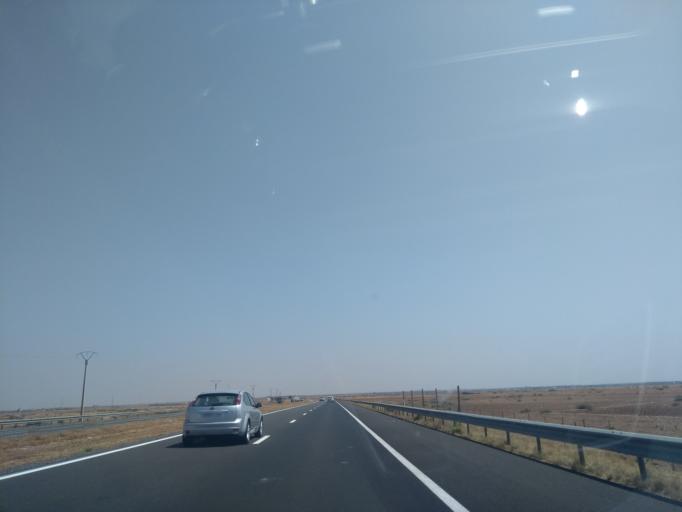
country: MA
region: Marrakech-Tensift-Al Haouz
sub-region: Kelaa-Des-Sraghna
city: Sidi Bou Othmane
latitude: 31.9255
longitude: -8.0213
